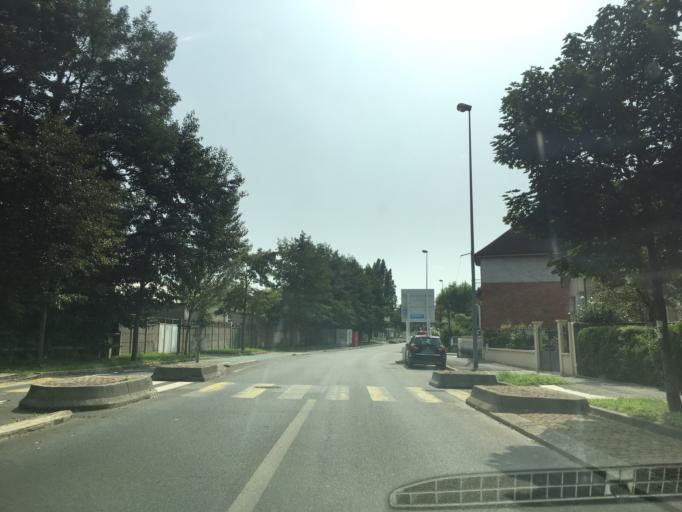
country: FR
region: Ile-de-France
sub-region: Departement du Val-de-Marne
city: Creteil
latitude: 48.8014
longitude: 2.4673
